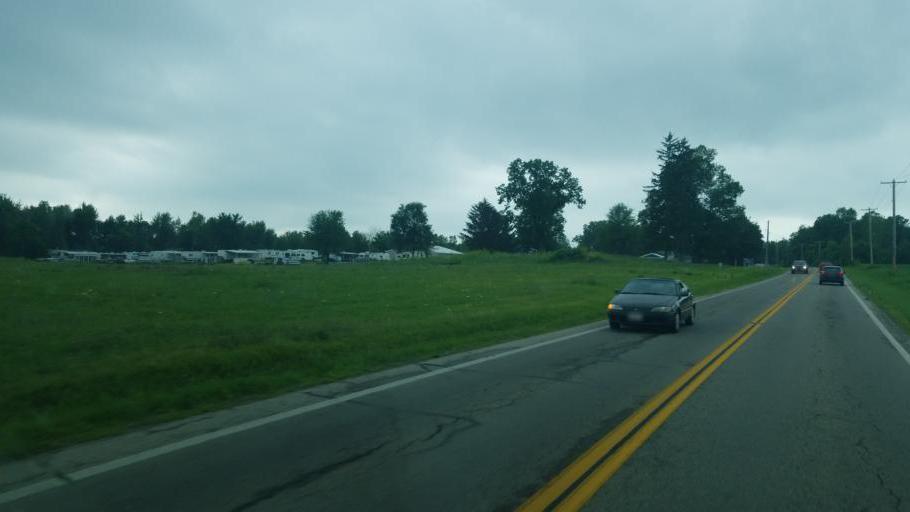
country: US
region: Ohio
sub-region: Logan County
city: Russells Point
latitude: 40.5286
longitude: -83.8494
